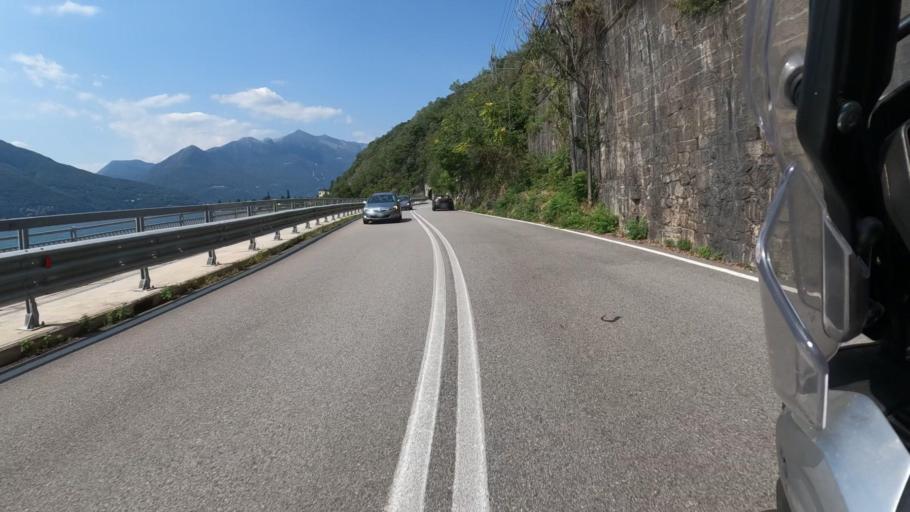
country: IT
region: Lombardy
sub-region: Provincia di Varese
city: Agra
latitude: 46.0287
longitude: 8.7506
